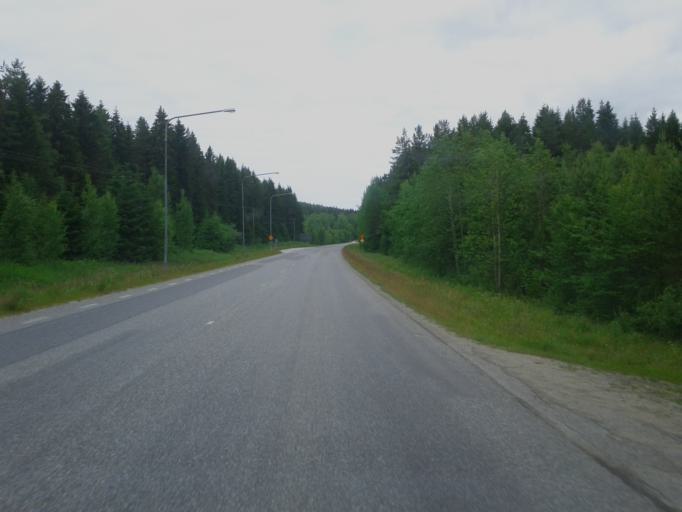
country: SE
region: Vaesternorrland
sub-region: OErnskoeldsviks Kommun
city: Bjasta
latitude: 63.2080
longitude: 18.4826
